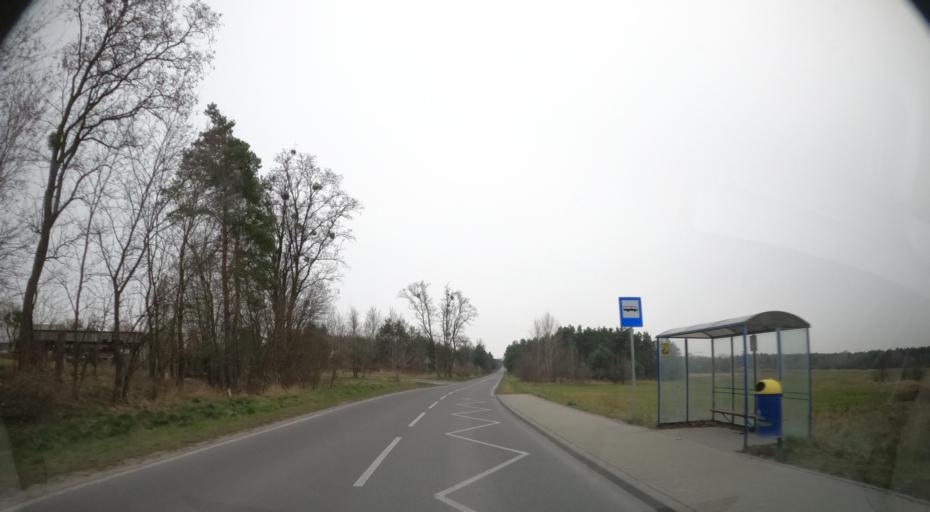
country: PL
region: Masovian Voivodeship
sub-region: Powiat radomski
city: Jastrzebia
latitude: 51.4690
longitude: 21.2002
